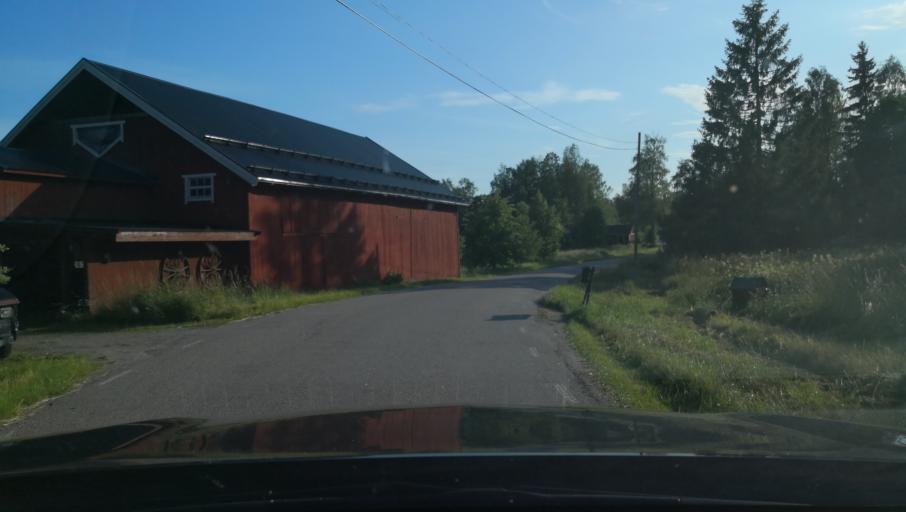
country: SE
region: Uppsala
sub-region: Osthammars Kommun
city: Osterbybruk
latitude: 60.0204
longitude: 17.9497
